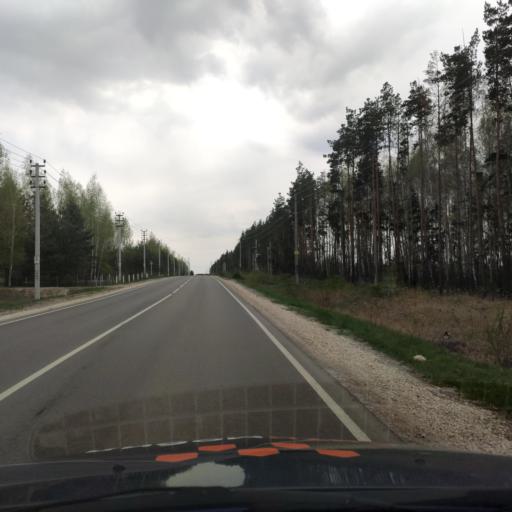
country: RU
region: Voronezj
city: Podgornoye
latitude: 51.8650
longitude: 39.1699
